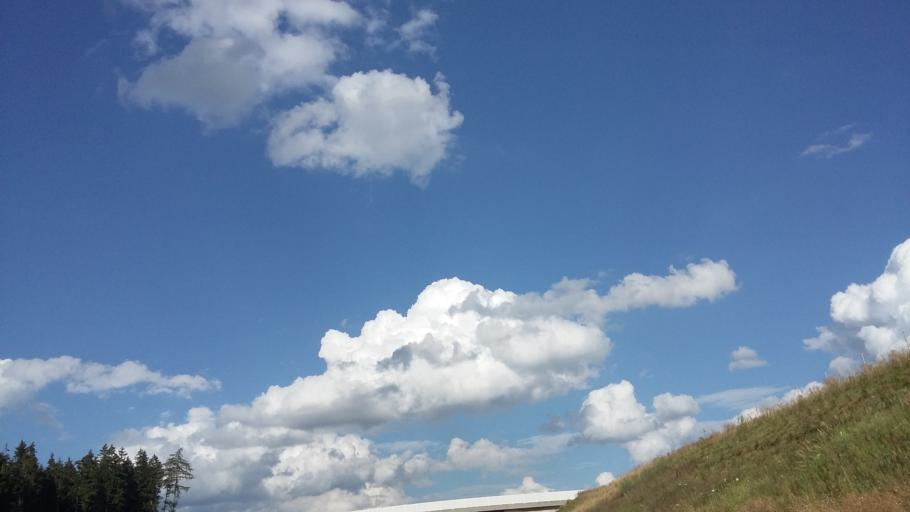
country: DE
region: Bavaria
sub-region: Swabia
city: Zusmarshausen
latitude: 48.4101
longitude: 10.6150
